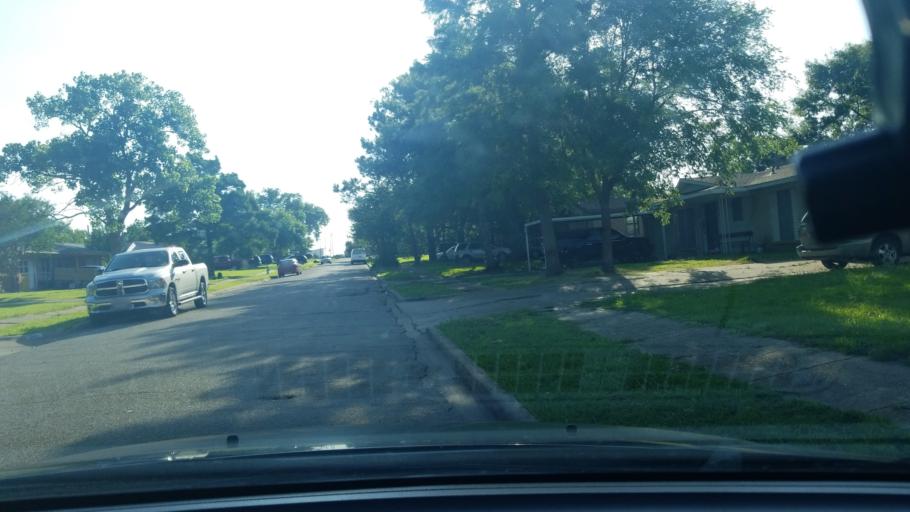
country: US
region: Texas
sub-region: Dallas County
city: Mesquite
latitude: 32.8126
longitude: -96.6410
